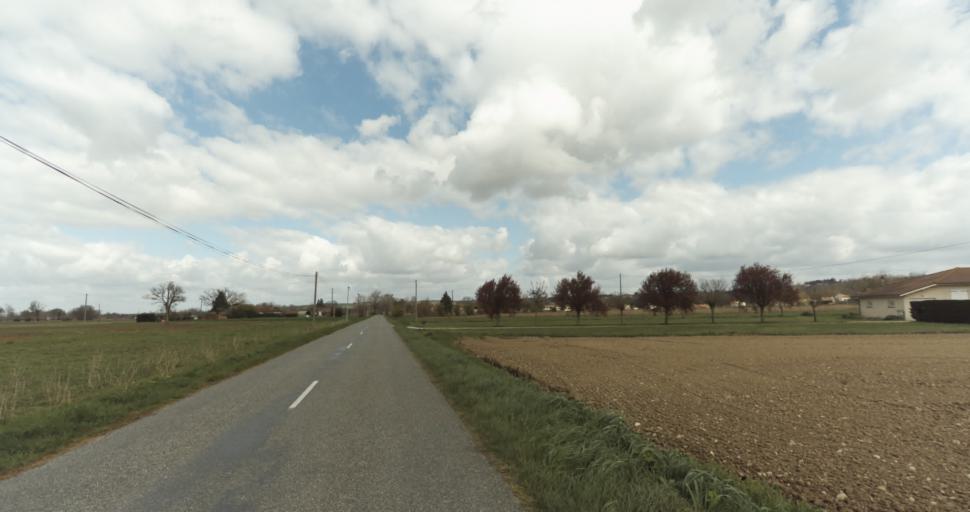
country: FR
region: Midi-Pyrenees
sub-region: Departement de la Haute-Garonne
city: Auterive
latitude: 43.3320
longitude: 1.4785
